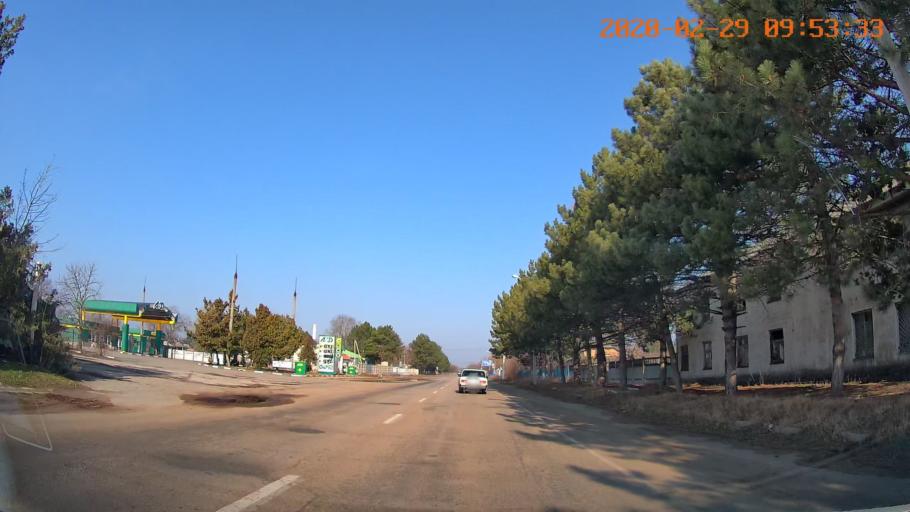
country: MD
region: Telenesti
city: Slobozia
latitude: 46.7227
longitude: 29.7211
